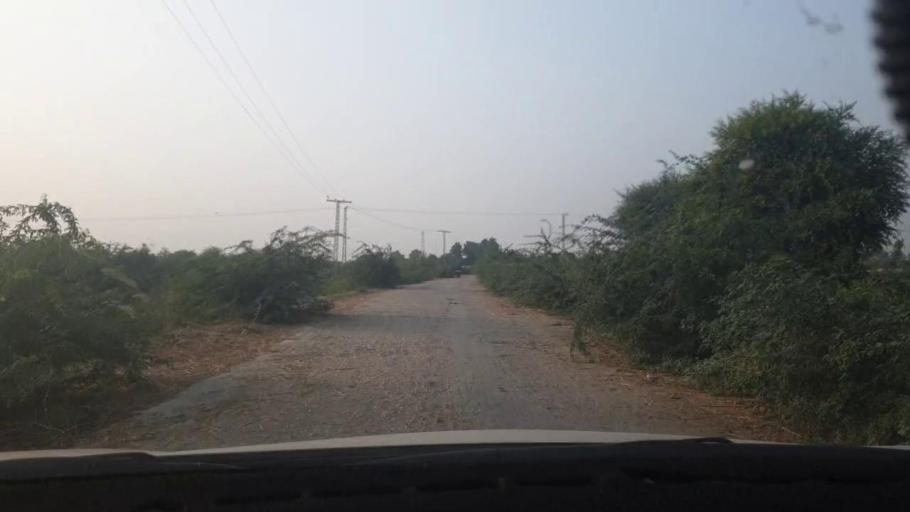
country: PK
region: Sindh
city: Bulri
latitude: 24.8569
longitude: 68.3359
